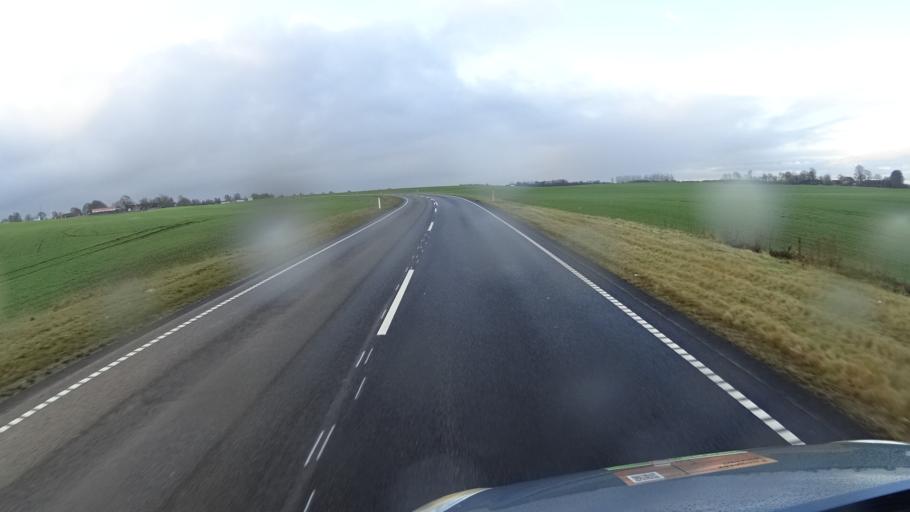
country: DK
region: South Denmark
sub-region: Vejle Kommune
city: Jelling
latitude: 55.7647
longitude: 9.4178
